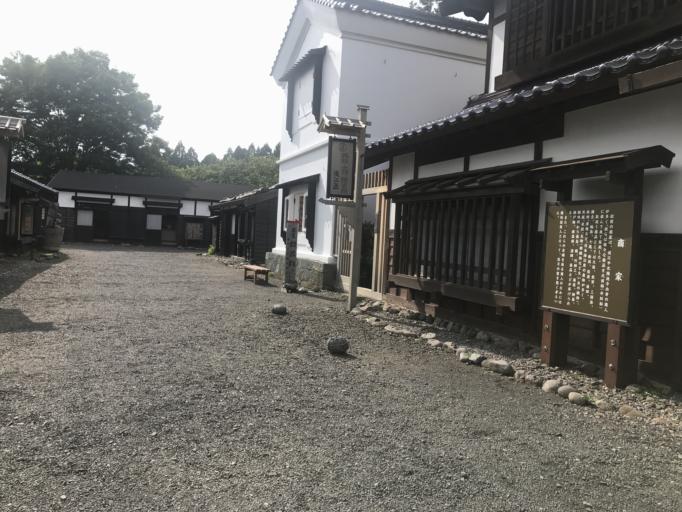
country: JP
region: Hokkaido
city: Kamiiso
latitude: 41.4342
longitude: 140.1042
